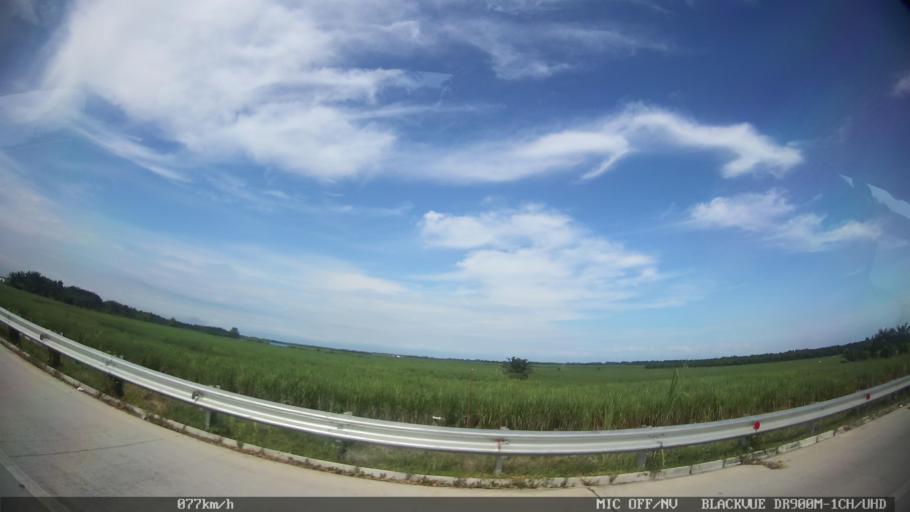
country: ID
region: North Sumatra
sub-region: Kabupaten Langkat
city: Stabat
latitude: 3.7225
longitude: 98.4932
